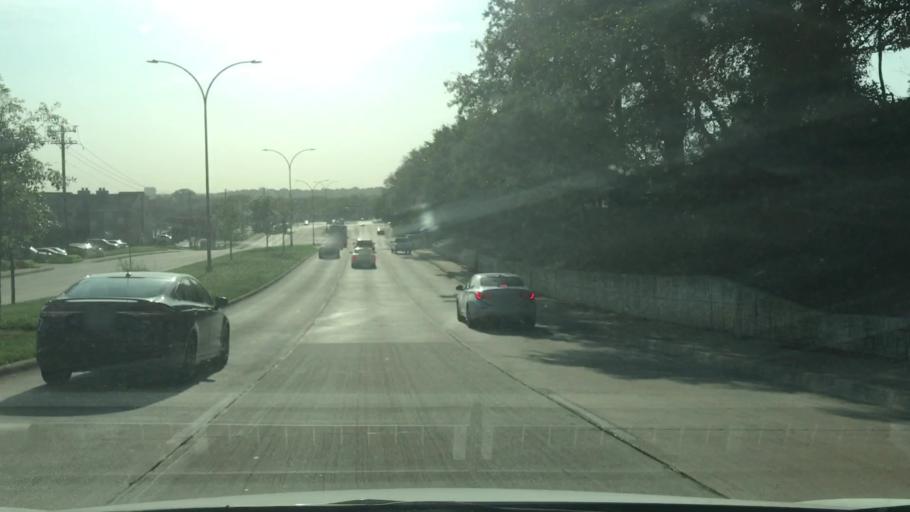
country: US
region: Texas
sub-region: Tarrant County
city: Arlington
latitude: 32.7845
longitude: -97.0991
